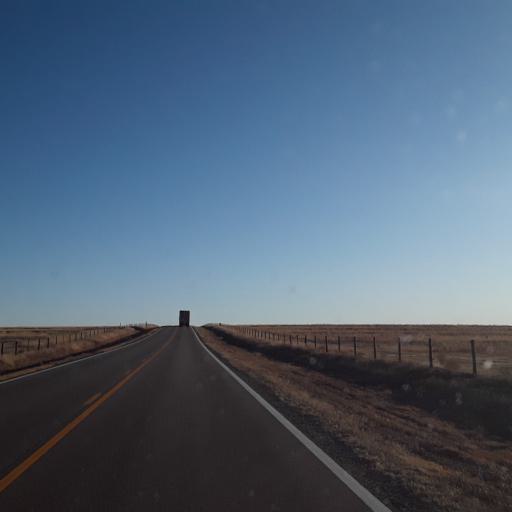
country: US
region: Kansas
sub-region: Wallace County
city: Sharon Springs
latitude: 39.0268
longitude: -101.7387
